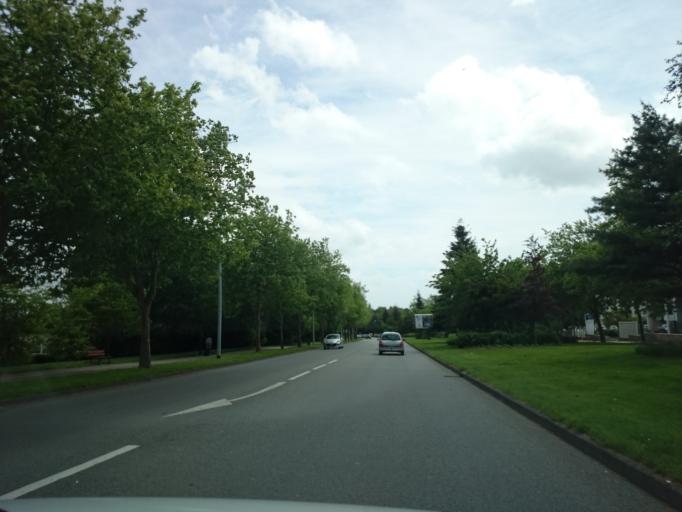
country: FR
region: Brittany
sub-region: Departement du Morbihan
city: Vannes
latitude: 47.6500
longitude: -2.7829
